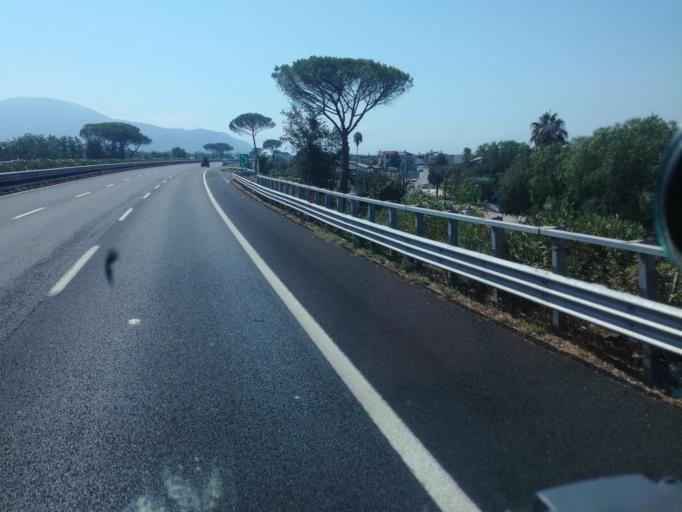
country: IT
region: Campania
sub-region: Provincia di Napoli
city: Nola
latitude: 40.9110
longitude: 14.5277
